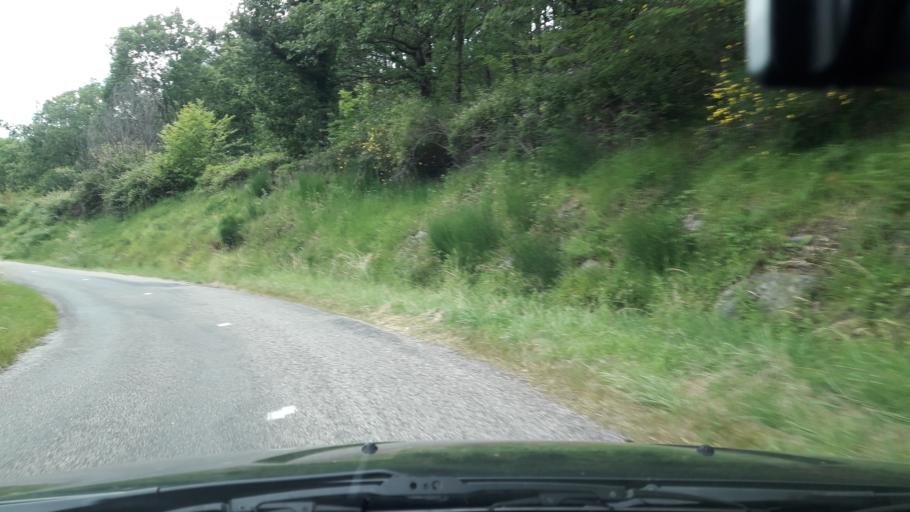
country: FR
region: Rhone-Alpes
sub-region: Departement de l'Ardeche
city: Vesseaux
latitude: 44.6491
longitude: 4.5138
